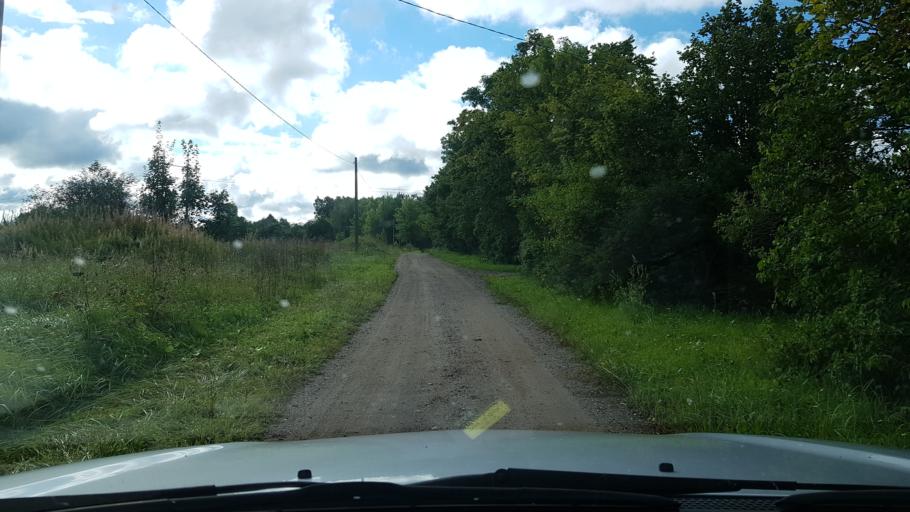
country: EE
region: Harju
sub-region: Rae vald
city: Vaida
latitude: 59.2699
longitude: 25.0260
